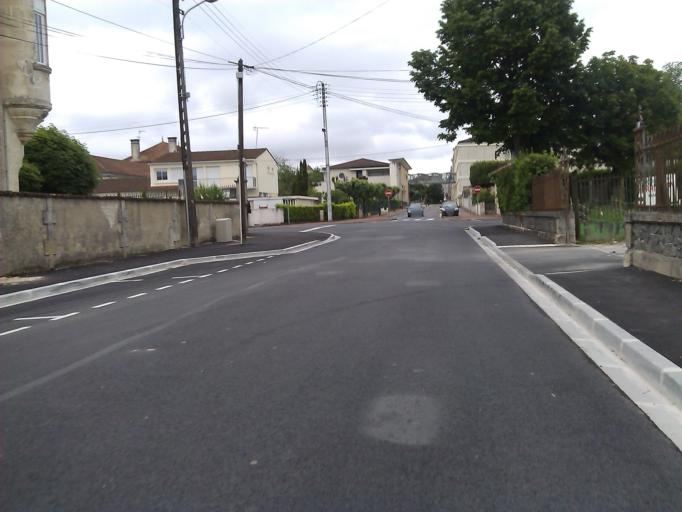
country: FR
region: Poitou-Charentes
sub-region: Departement de la Charente
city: Barbezieux-Saint-Hilaire
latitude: 45.4747
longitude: -0.1474
